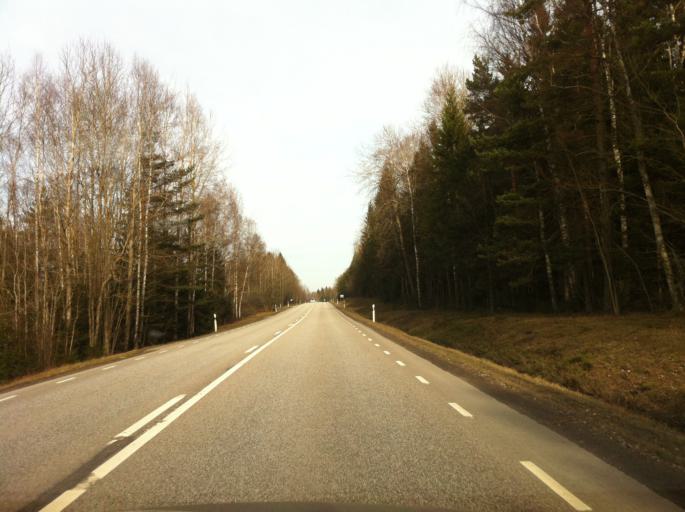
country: SE
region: Vaestra Goetaland
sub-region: Gullspangs Kommun
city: Gullspang
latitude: 58.9696
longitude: 14.0700
